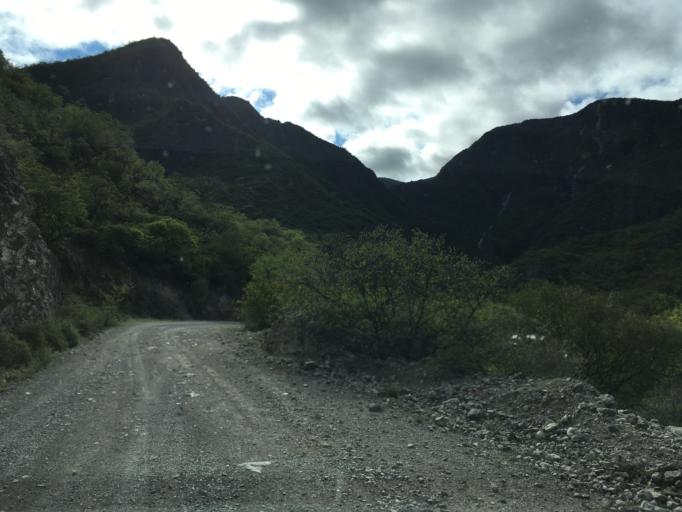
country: MX
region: Hidalgo
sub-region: Metztitlan
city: Fontezuelas
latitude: 20.6371
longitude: -98.9317
